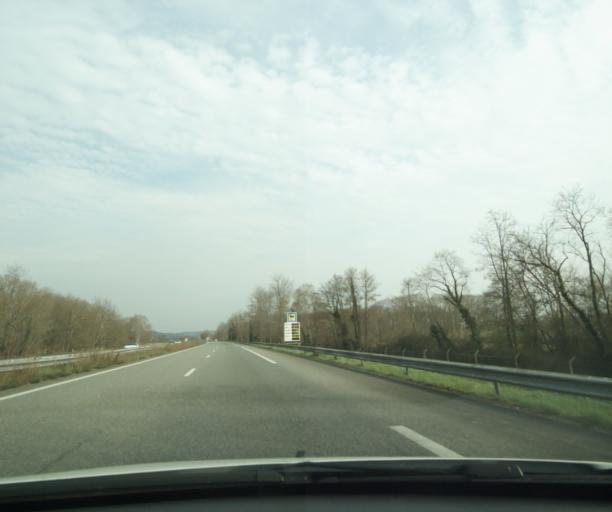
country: FR
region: Aquitaine
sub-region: Departement des Pyrenees-Atlantiques
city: Mont
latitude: 43.4241
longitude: -0.6129
